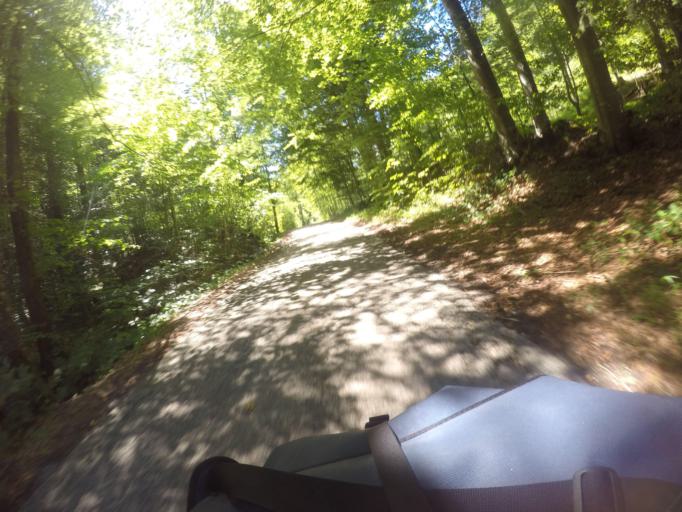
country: AT
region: Tyrol
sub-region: Politischer Bezirk Reutte
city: Vils
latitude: 47.5611
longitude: 10.6467
